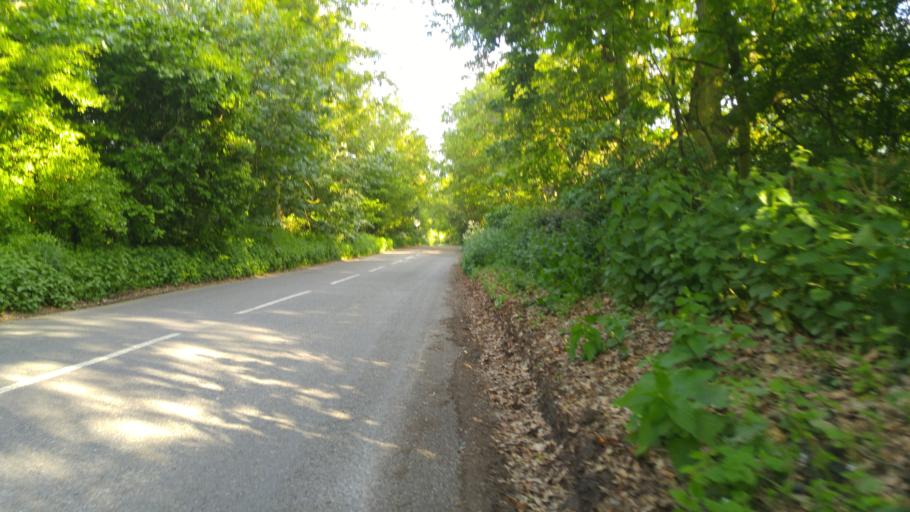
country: GB
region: England
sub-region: Essex
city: Tiptree
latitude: 51.8321
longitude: 0.7475
